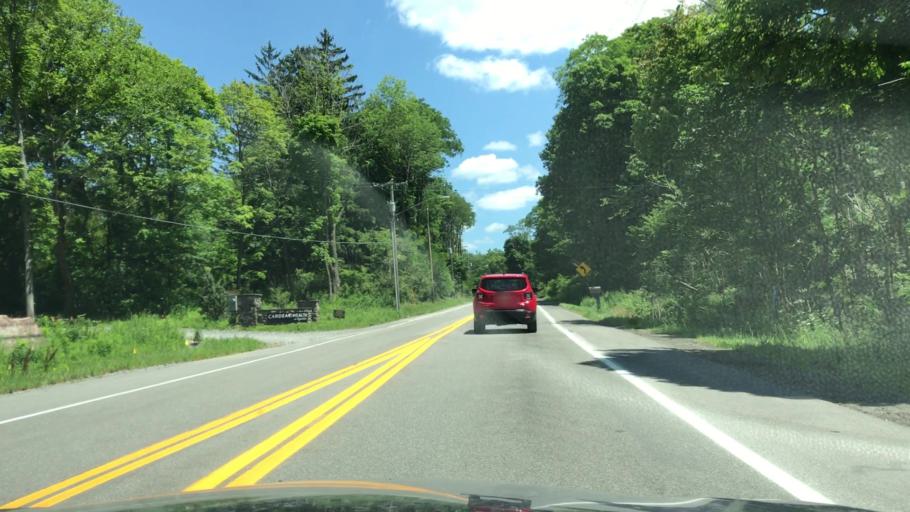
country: US
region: New York
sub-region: Erie County
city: East Aurora
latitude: 42.7674
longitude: -78.5876
